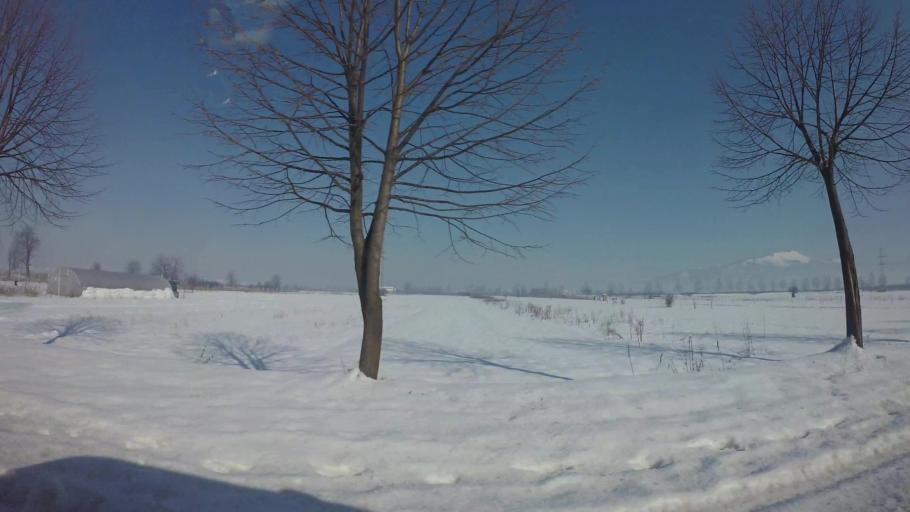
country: BA
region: Federation of Bosnia and Herzegovina
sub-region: Kanton Sarajevo
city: Sarajevo
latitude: 43.8024
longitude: 18.3072
